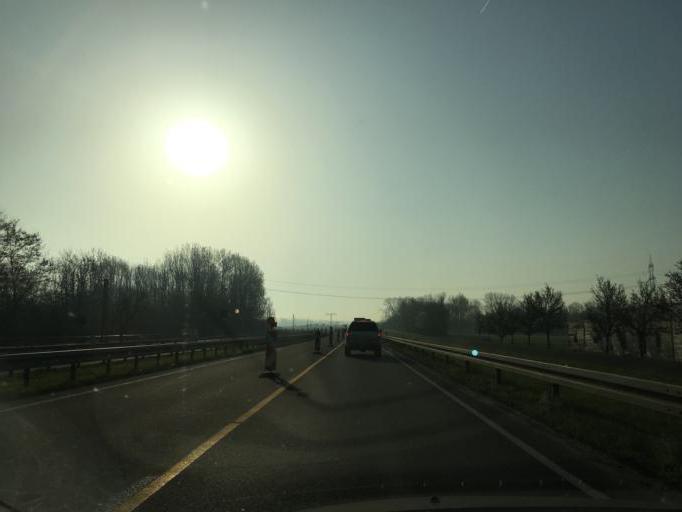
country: DE
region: Saxony
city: Rotha
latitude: 51.1981
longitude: 12.4316
